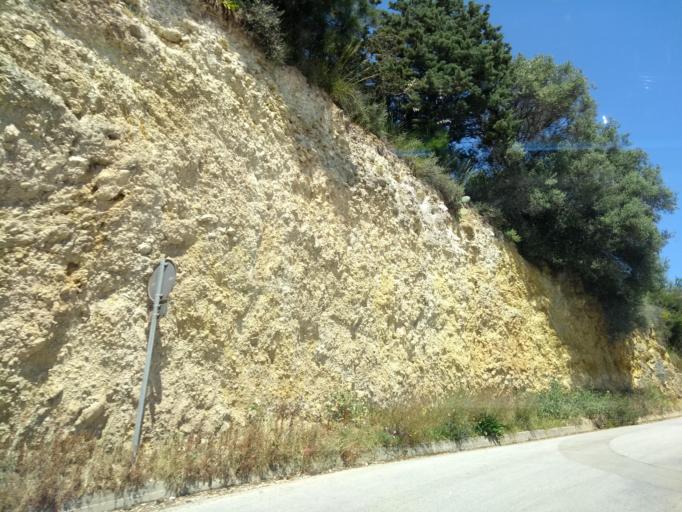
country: IT
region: Sicily
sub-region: Trapani
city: Castellammare del Golfo
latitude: 38.0564
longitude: 12.8357
